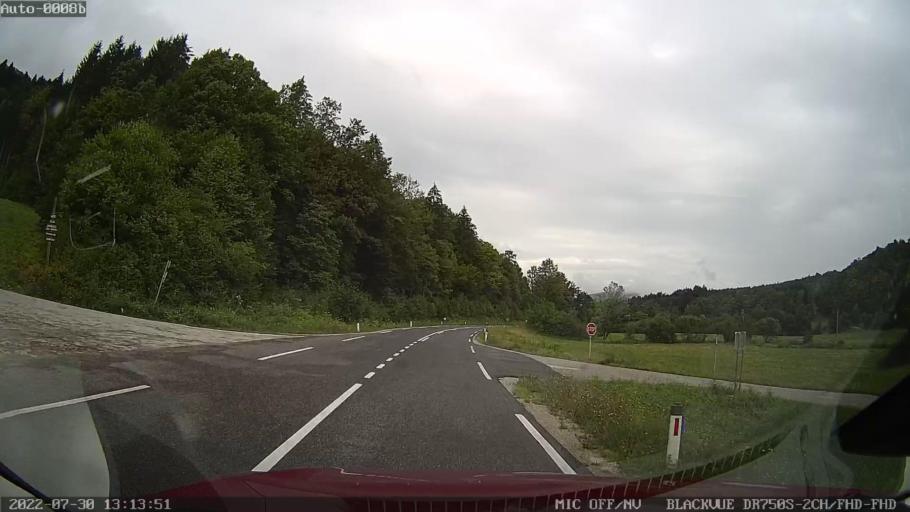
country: SI
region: Dolenjske Toplice
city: Dolenjske Toplice
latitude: 45.7245
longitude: 15.0529
